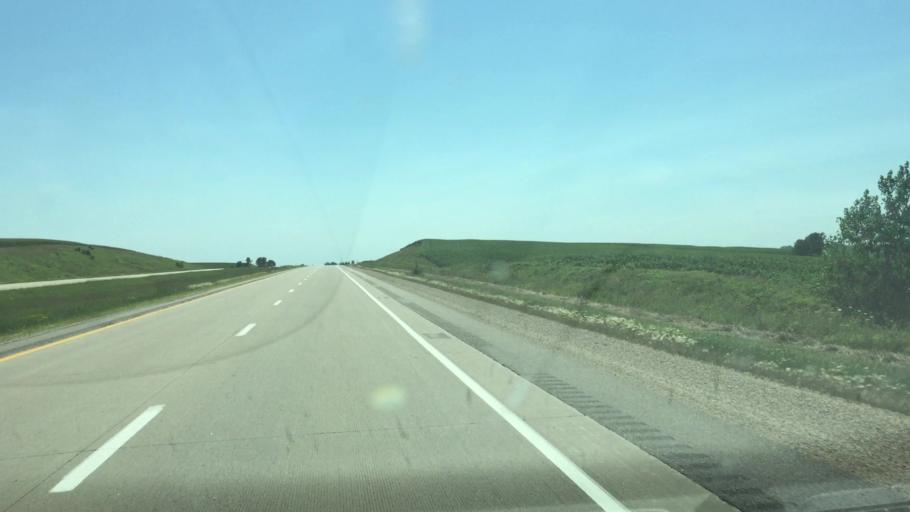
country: US
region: Iowa
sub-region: Dubuque County
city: Peosta
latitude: 42.3568
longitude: -90.8163
